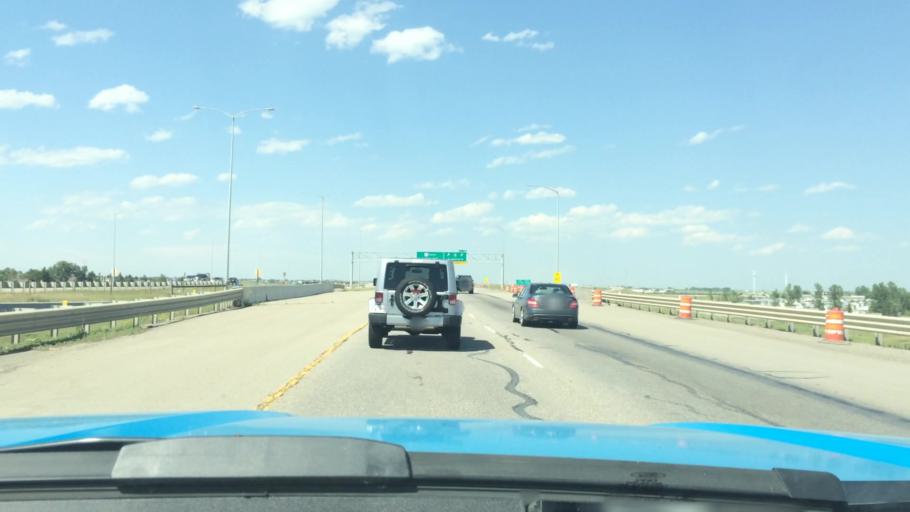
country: CA
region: Alberta
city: Chestermere
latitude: 51.0561
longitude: -113.9202
